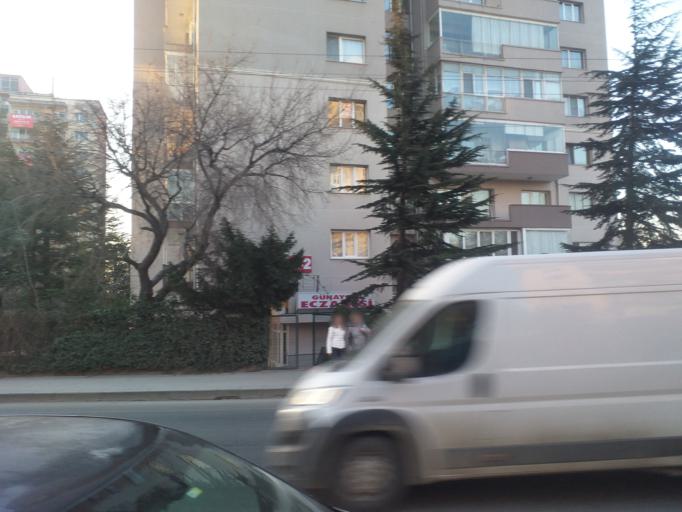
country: TR
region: Ankara
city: Ankara
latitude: 39.9569
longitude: 32.8199
